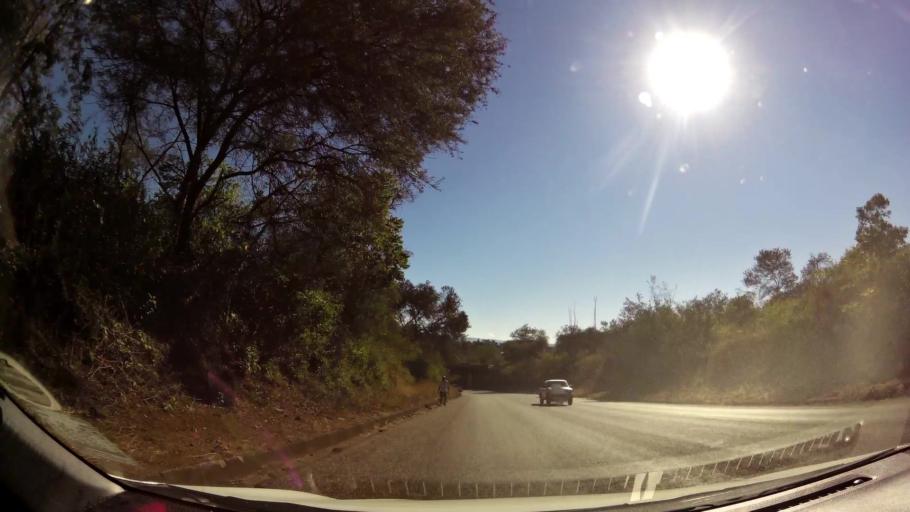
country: ZA
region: Limpopo
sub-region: Mopani District Municipality
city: Tzaneen
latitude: -23.8521
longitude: 30.1689
